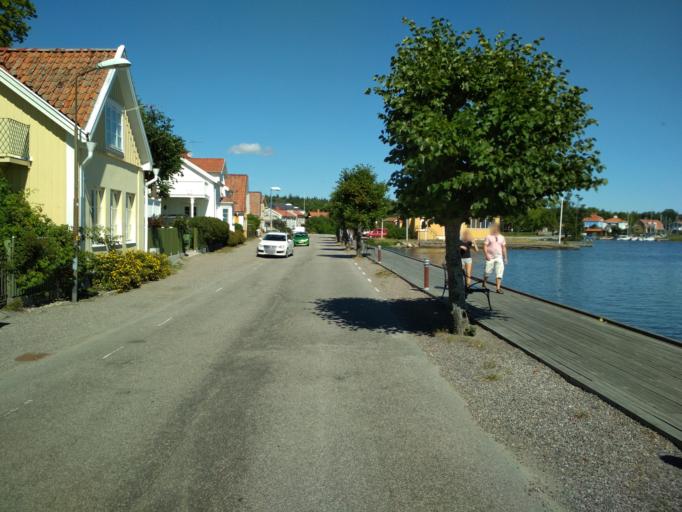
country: SE
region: Soedermanland
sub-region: Strangnas Kommun
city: Mariefred
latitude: 59.2582
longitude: 17.2253
